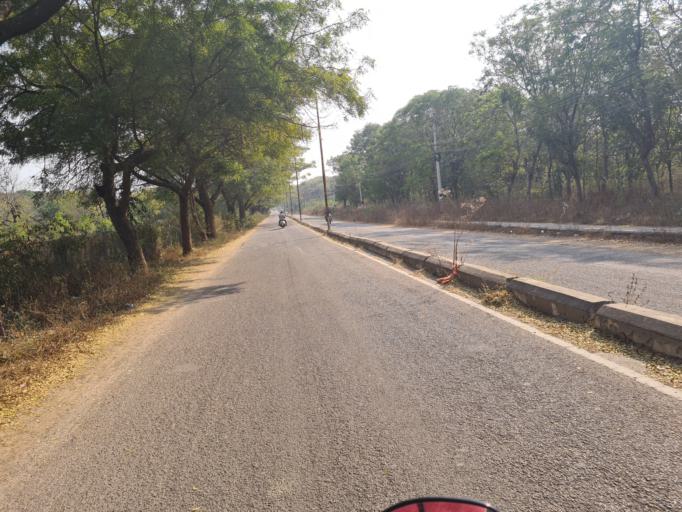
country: IN
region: Telangana
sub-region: Medak
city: Serilingampalle
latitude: 17.4908
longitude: 78.2978
